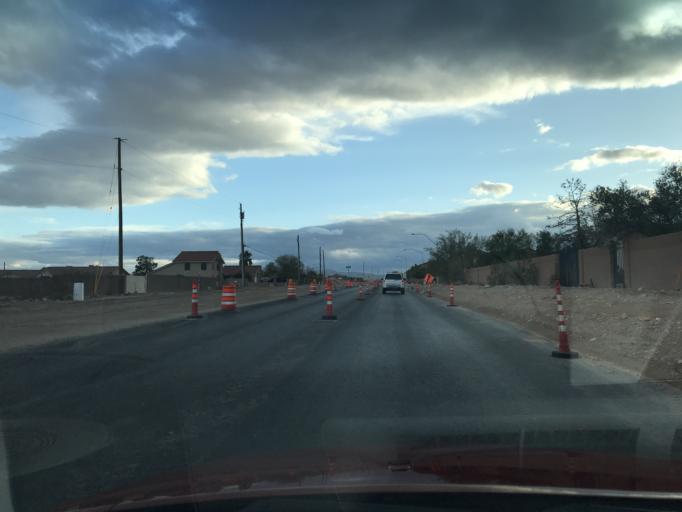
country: US
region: Nevada
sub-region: Clark County
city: Enterprise
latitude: 36.0344
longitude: -115.2790
